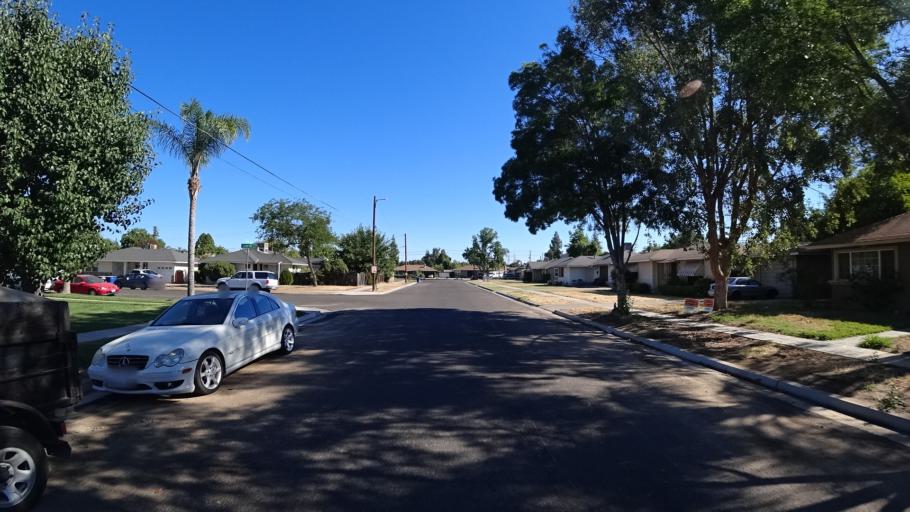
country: US
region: California
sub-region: Fresno County
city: Fresno
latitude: 36.7921
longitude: -119.8314
